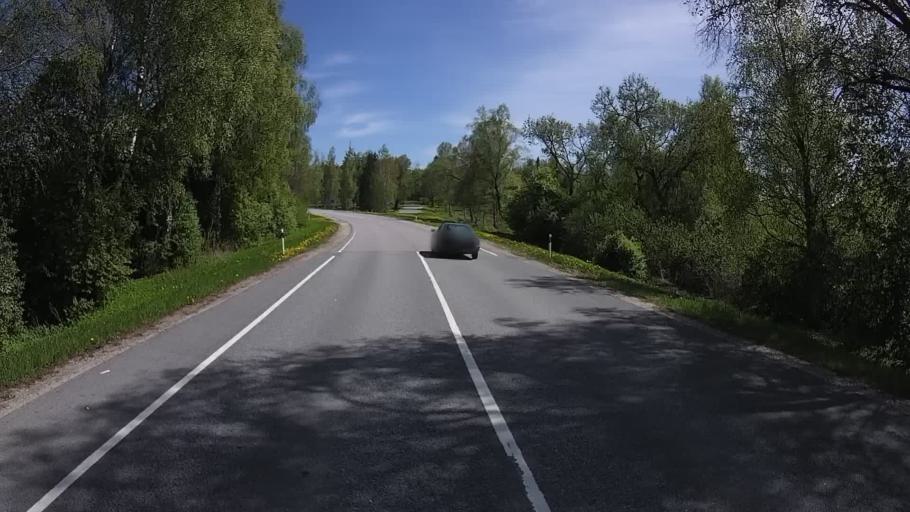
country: LV
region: Apes Novads
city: Ape
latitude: 57.6177
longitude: 26.6077
